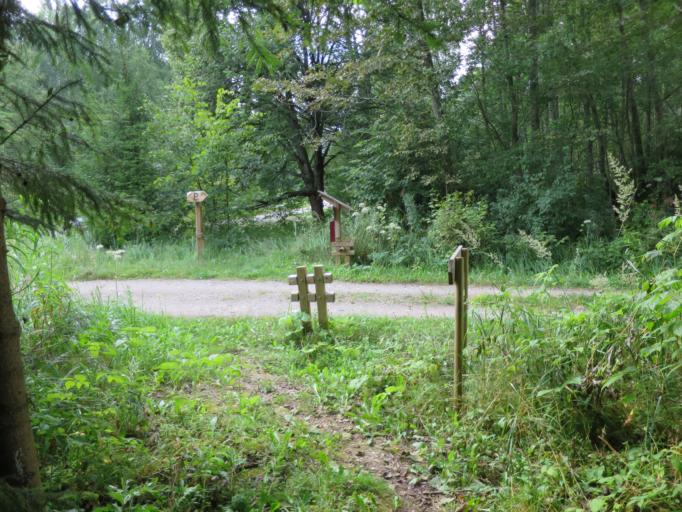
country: LV
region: Amatas Novads
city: Drabesi
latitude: 57.2219
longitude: 25.2239
